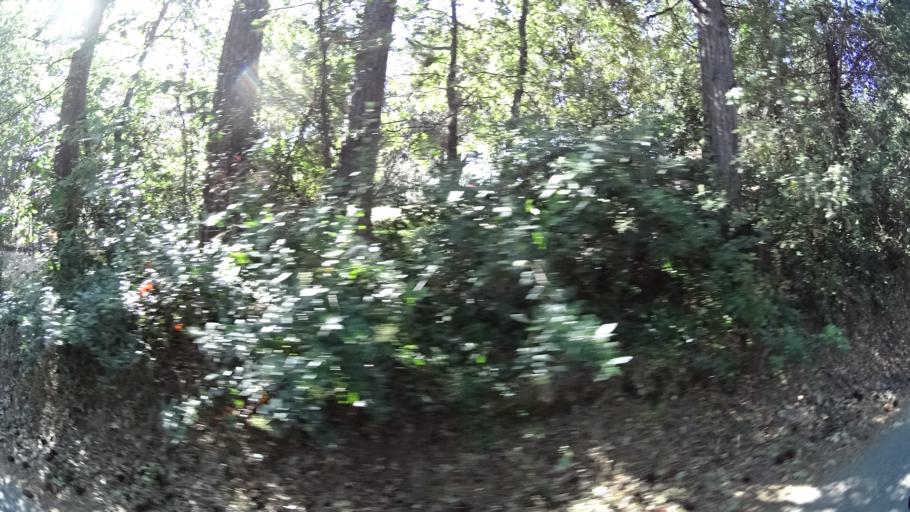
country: US
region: California
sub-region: Amador County
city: Pioneer
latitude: 38.4073
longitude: -120.5575
